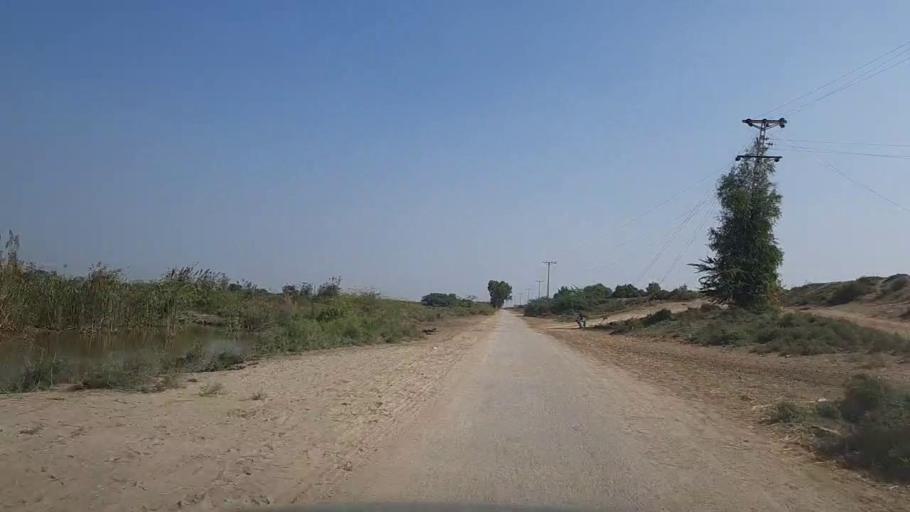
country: PK
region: Sindh
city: Thatta
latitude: 24.5869
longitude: 67.9285
